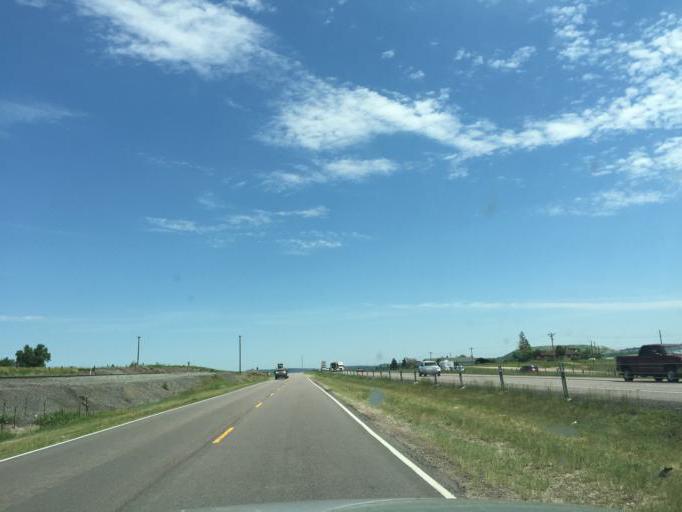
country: US
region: Colorado
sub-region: Douglas County
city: Castle Rock
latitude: 39.3083
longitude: -104.8873
